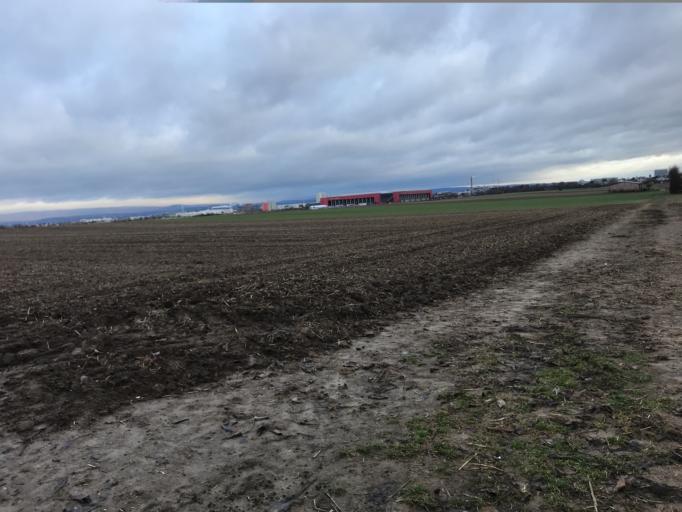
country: DE
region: Rheinland-Pfalz
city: Klein-Winternheim
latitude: 49.9762
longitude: 8.2159
